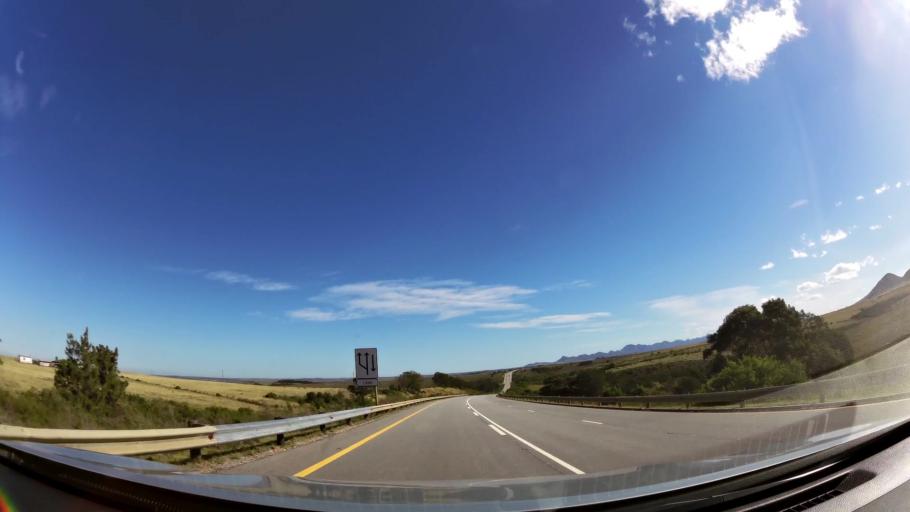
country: ZA
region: Eastern Cape
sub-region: Cacadu District Municipality
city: Kruisfontein
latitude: -34.0047
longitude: 24.6767
